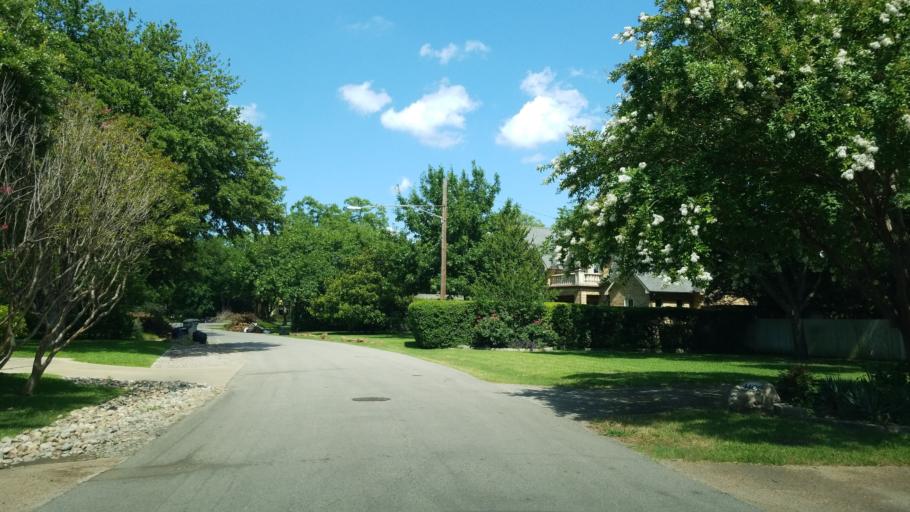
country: US
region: Texas
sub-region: Dallas County
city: University Park
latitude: 32.8856
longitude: -96.8349
